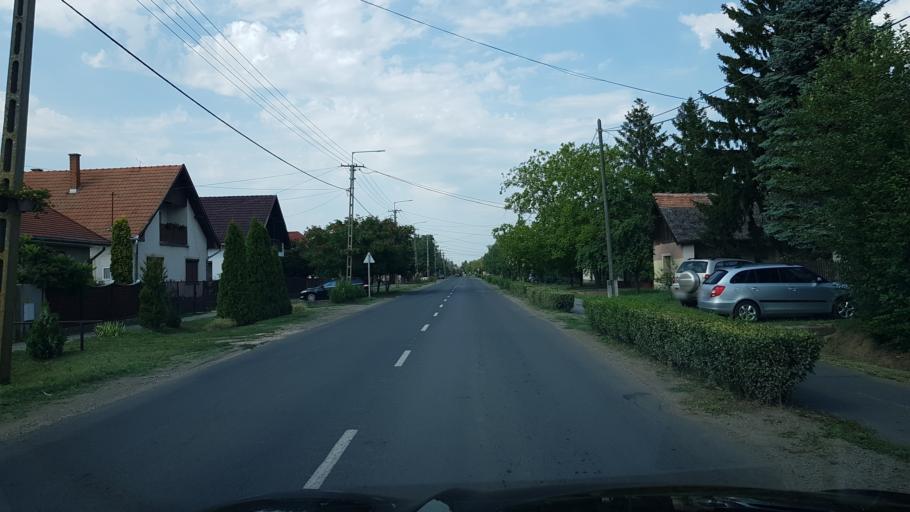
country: HU
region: Bekes
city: Fuzesgyarmat
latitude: 47.0977
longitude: 21.2073
